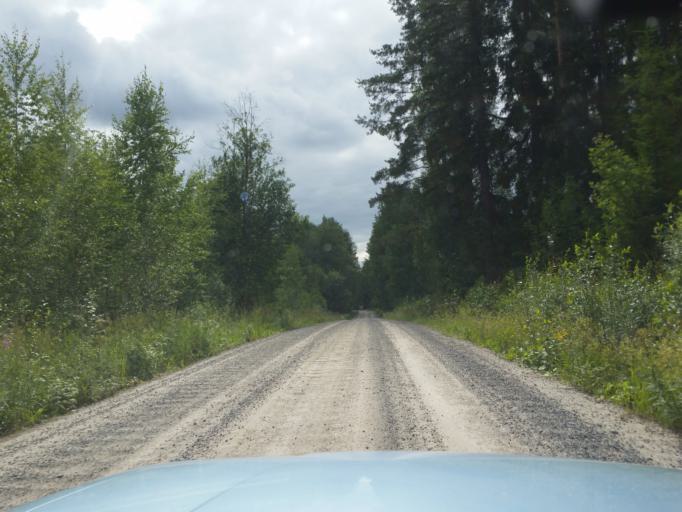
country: FI
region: Southern Savonia
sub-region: Savonlinna
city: Sulkava
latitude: 61.7196
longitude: 28.3109
